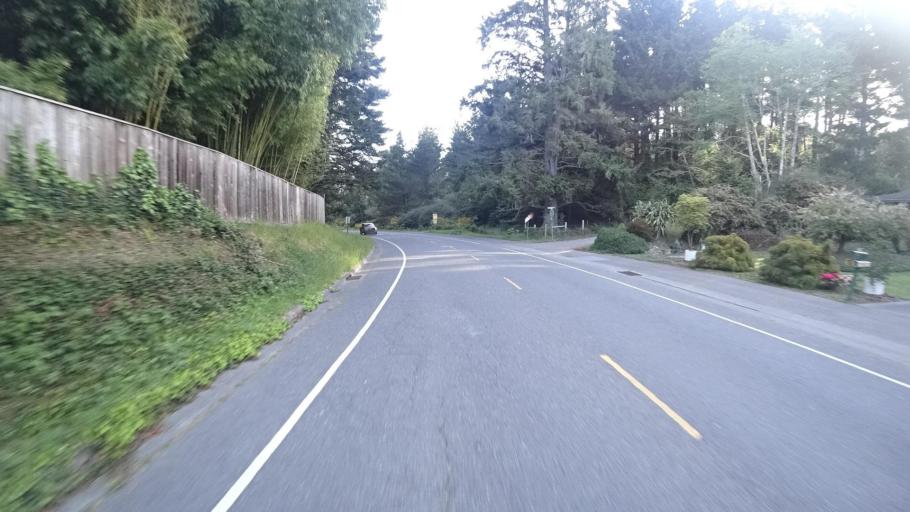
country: US
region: California
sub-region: Humboldt County
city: Humboldt Hill
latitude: 40.7229
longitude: -124.2012
